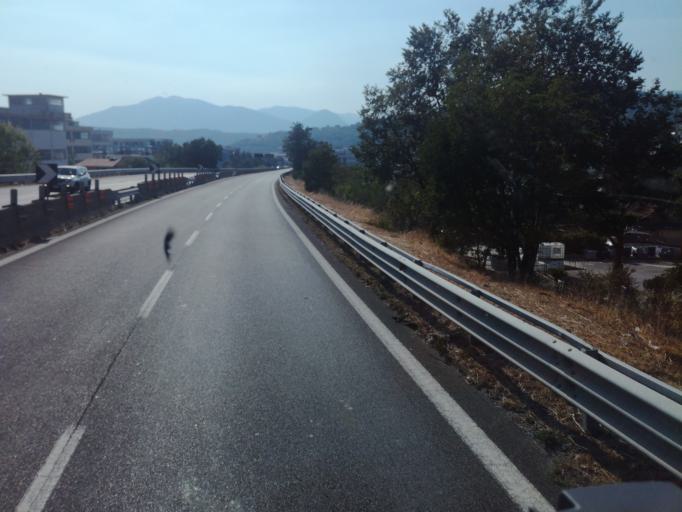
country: IT
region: Campania
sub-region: Provincia di Avellino
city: Solofra
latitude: 40.8335
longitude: 14.8341
